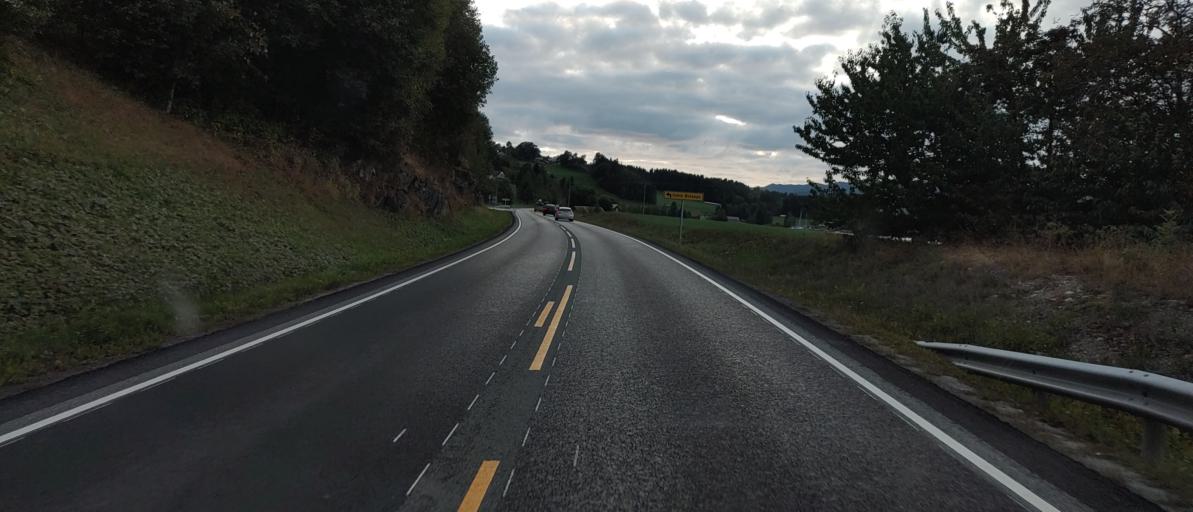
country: NO
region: More og Romsdal
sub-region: Molde
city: Hjelset
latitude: 62.7319
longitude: 7.3452
